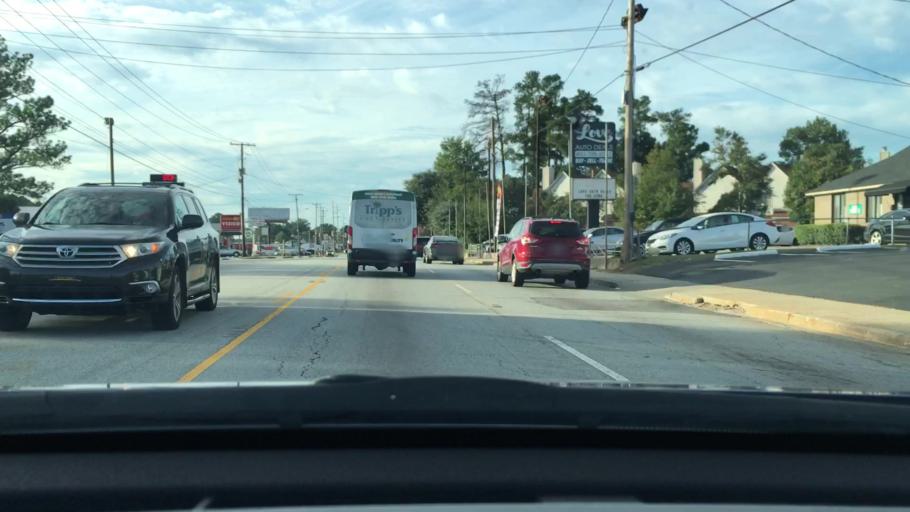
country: US
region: South Carolina
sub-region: Lexington County
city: Saint Andrews
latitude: 34.0462
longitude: -81.1015
